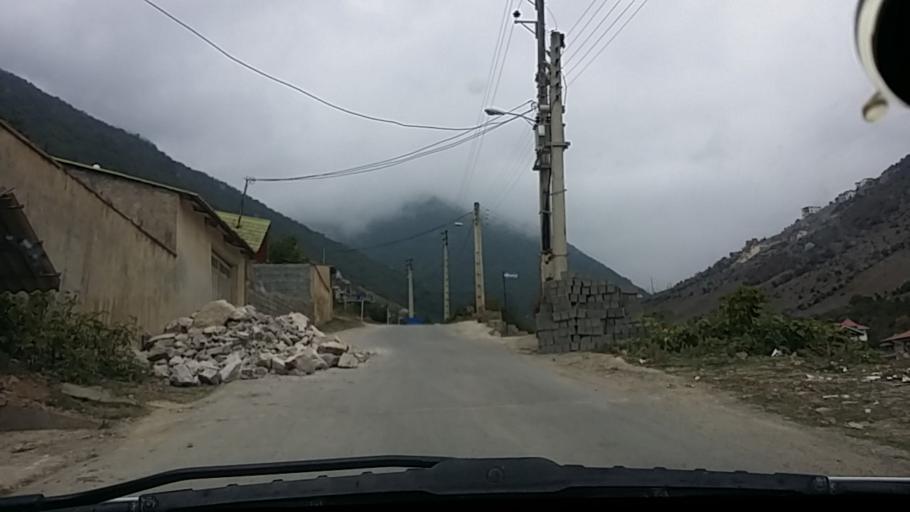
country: IR
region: Mazandaran
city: `Abbasabad
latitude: 36.4755
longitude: 51.1401
